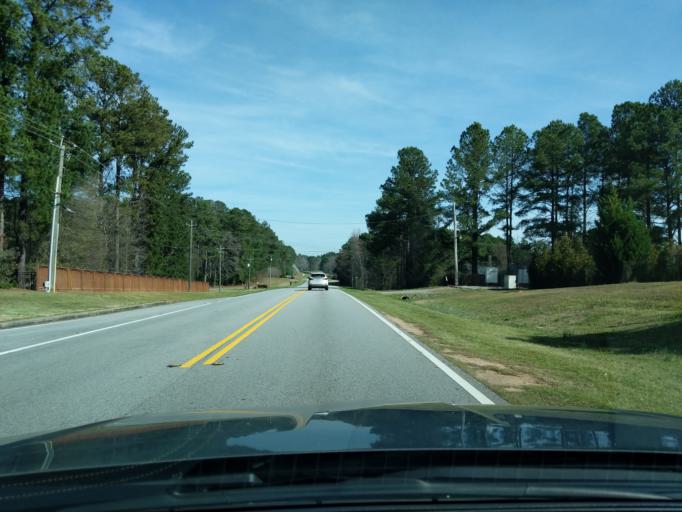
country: US
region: Georgia
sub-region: Columbia County
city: Evans
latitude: 33.5542
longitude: -82.1285
